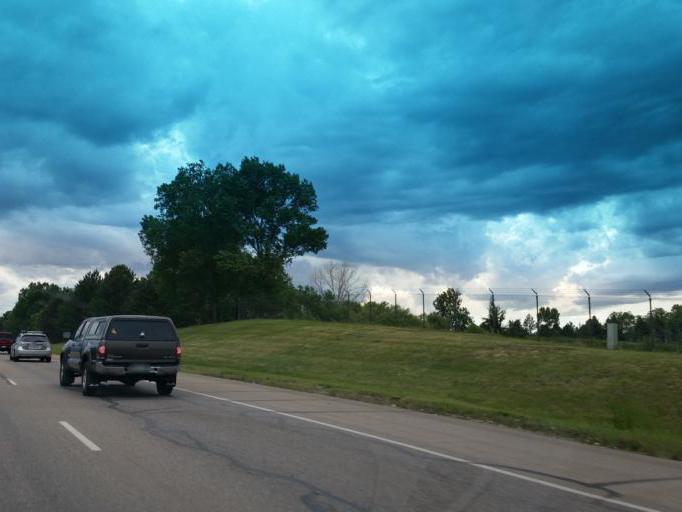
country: US
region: Colorado
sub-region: Larimer County
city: Fort Collins
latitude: 40.5234
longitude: -105.0058
